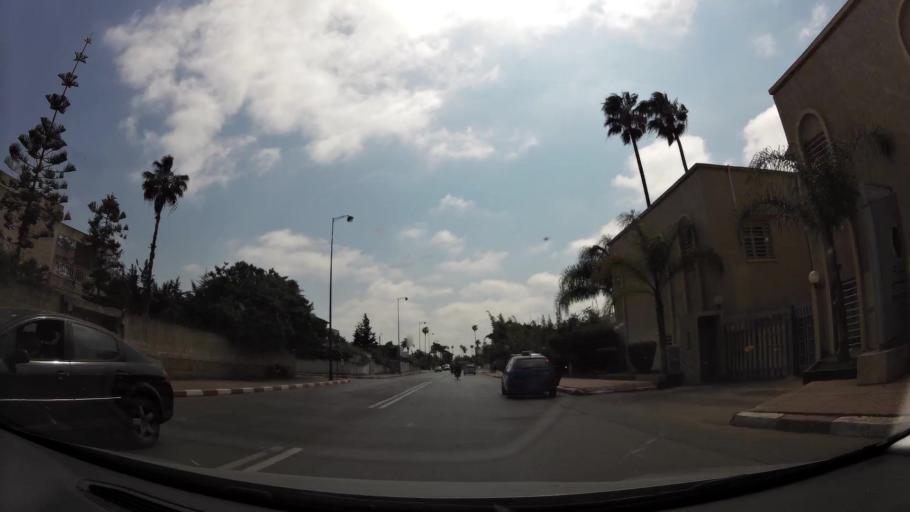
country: MA
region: Rabat-Sale-Zemmour-Zaer
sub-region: Rabat
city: Rabat
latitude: 33.9799
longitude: -6.8339
